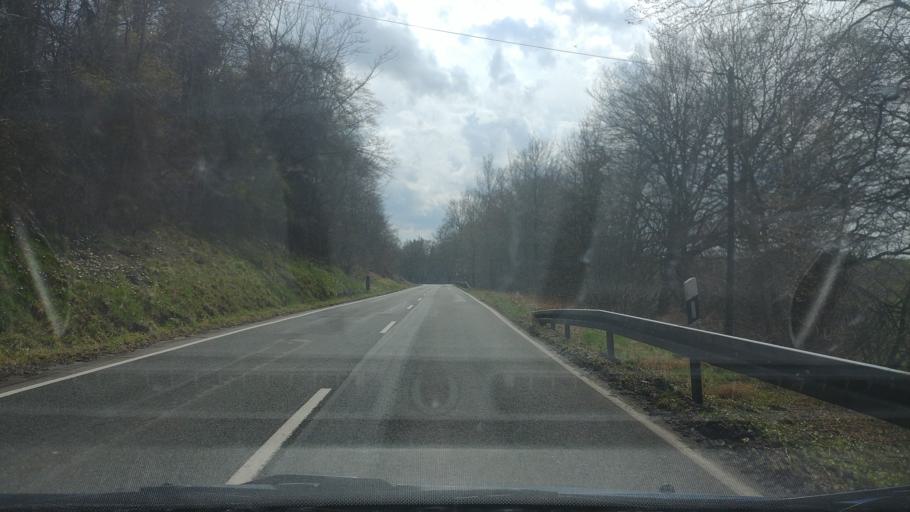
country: DE
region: Lower Saxony
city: Furstenberg
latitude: 51.7454
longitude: 9.4042
